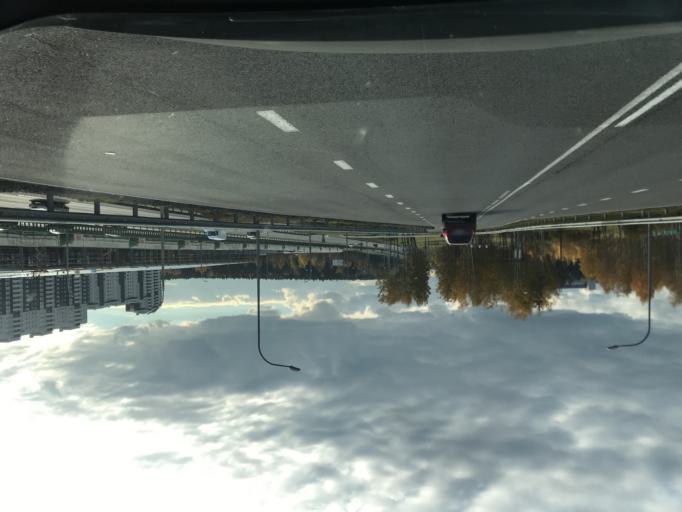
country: BY
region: Minsk
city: Borovlyany
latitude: 53.9344
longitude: 27.6765
